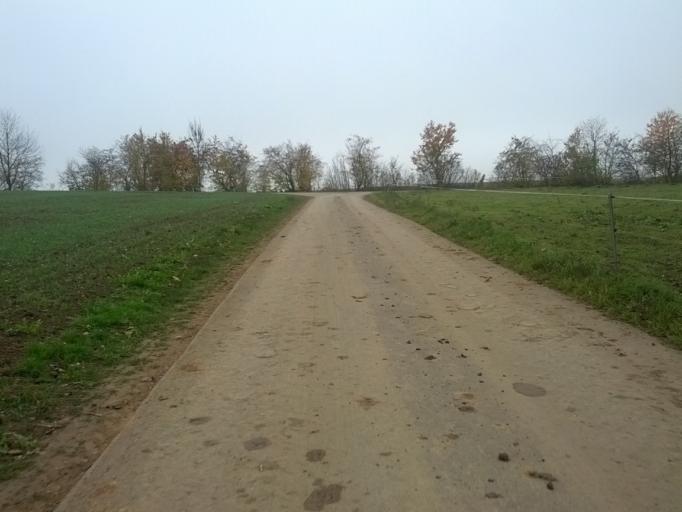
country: DE
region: Thuringia
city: Bischofroda
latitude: 50.9871
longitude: 10.3935
